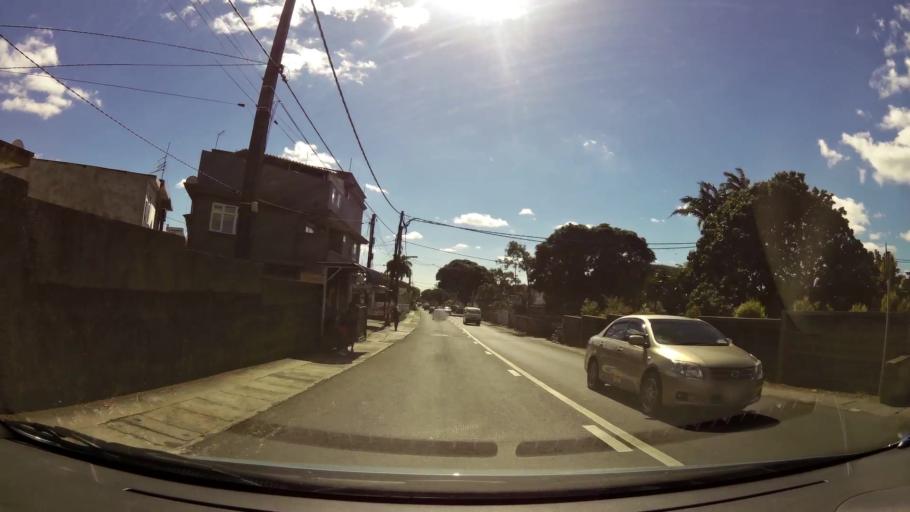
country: MU
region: Plaines Wilhems
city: Vacoas
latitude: -20.2871
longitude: 57.4809
